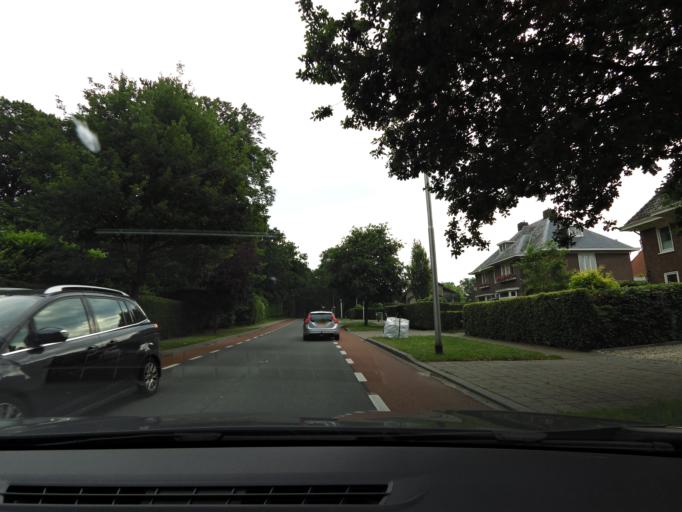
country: NL
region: Gelderland
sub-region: Gemeente Rheden
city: Velp
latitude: 52.0021
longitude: 5.9706
